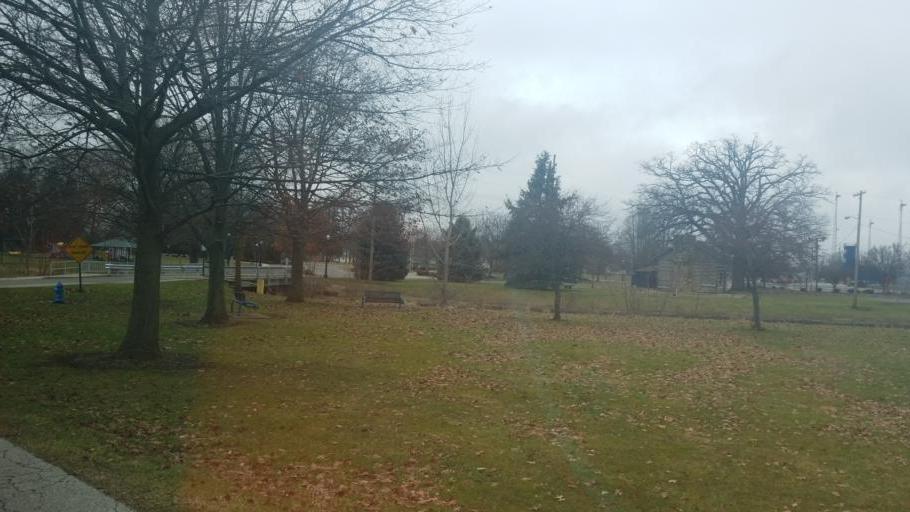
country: US
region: Ohio
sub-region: Crawford County
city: Galion
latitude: 40.7367
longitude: -82.7975
